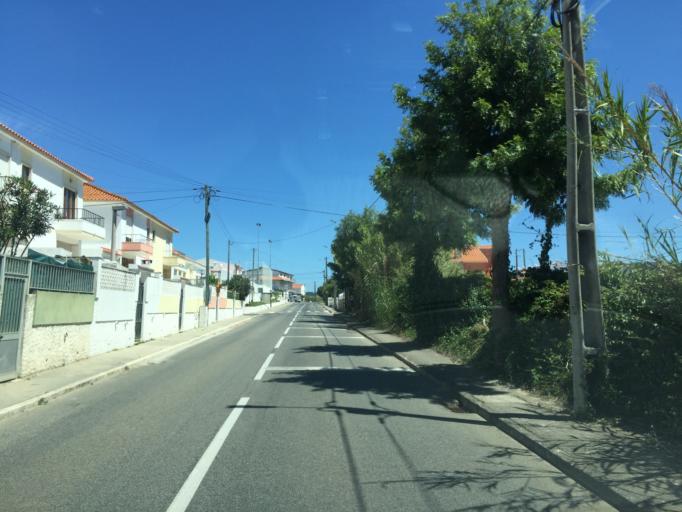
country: PT
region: Lisbon
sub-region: Torres Vedras
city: A dos Cunhados
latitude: 39.1814
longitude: -9.3147
